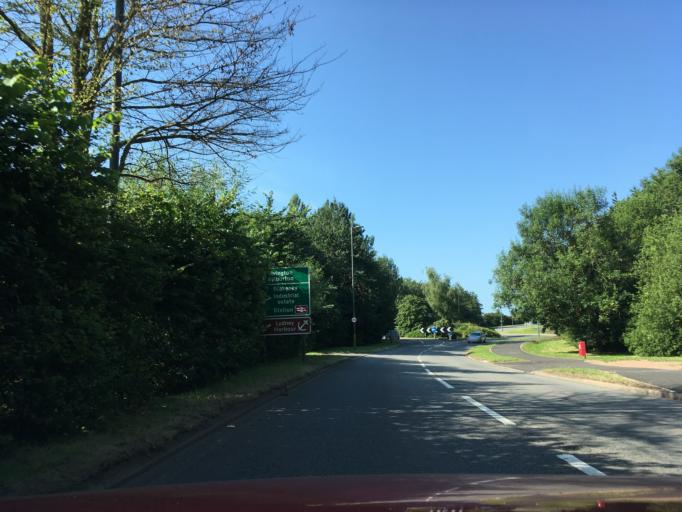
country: GB
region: England
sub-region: Gloucestershire
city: Lydney
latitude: 51.7183
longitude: -2.5436
